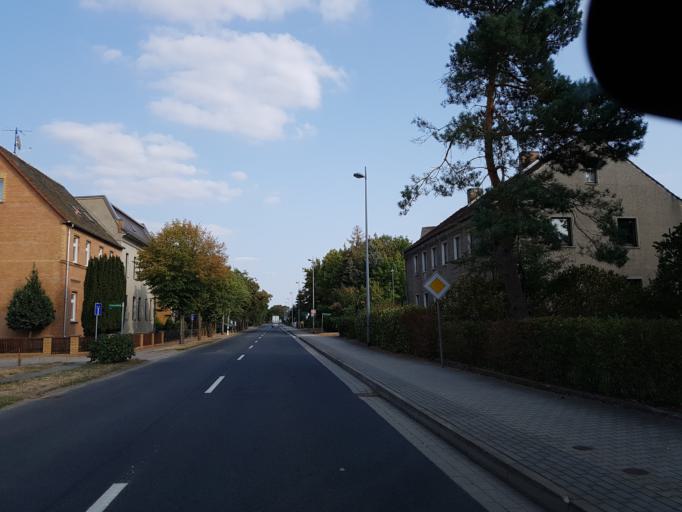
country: DE
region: Saxony-Anhalt
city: Pretzsch
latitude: 51.7188
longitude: 12.7995
